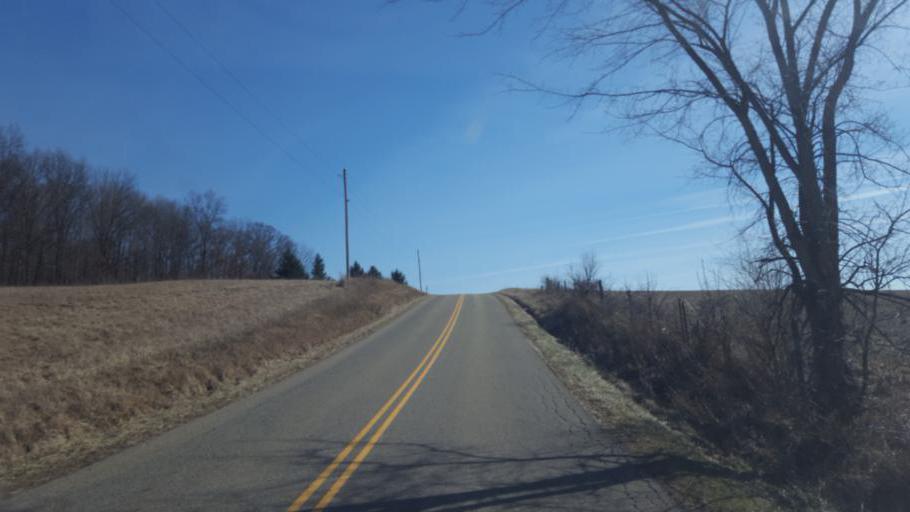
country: US
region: Ohio
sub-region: Knox County
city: Gambier
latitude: 40.4832
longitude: -82.3828
